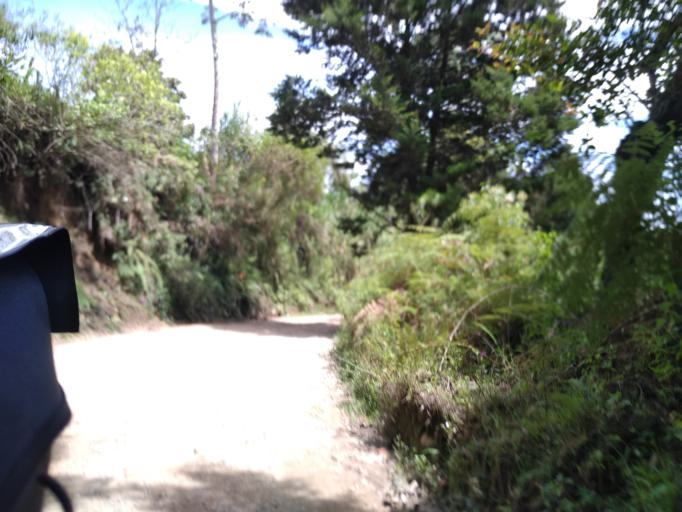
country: CO
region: Quindio
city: Salento
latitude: 4.6267
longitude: -75.5872
